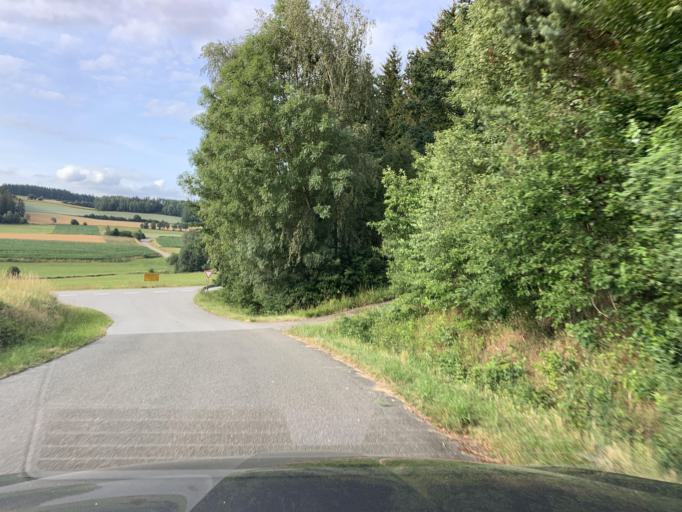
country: DE
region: Bavaria
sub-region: Upper Palatinate
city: Dieterskirchen
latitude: 49.3992
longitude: 12.4387
